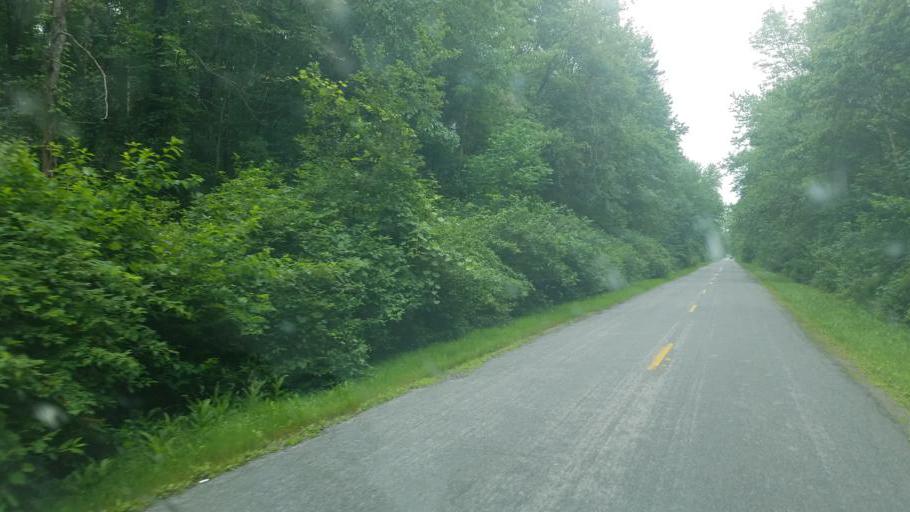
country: US
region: Ohio
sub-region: Trumbull County
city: Cortland
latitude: 41.4355
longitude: -80.7773
